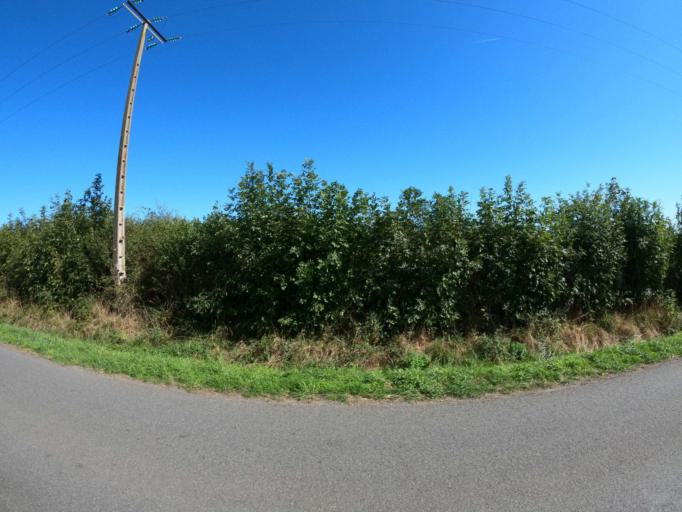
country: FR
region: Limousin
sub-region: Departement de la Haute-Vienne
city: Le Dorat
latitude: 46.2422
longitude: 1.0525
